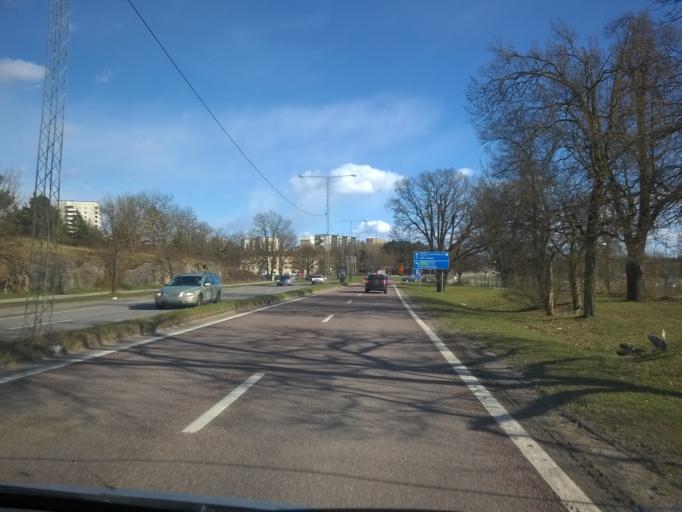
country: SE
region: Stockholm
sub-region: Jarfalla Kommun
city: Jakobsberg
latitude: 59.3670
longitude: 17.8578
